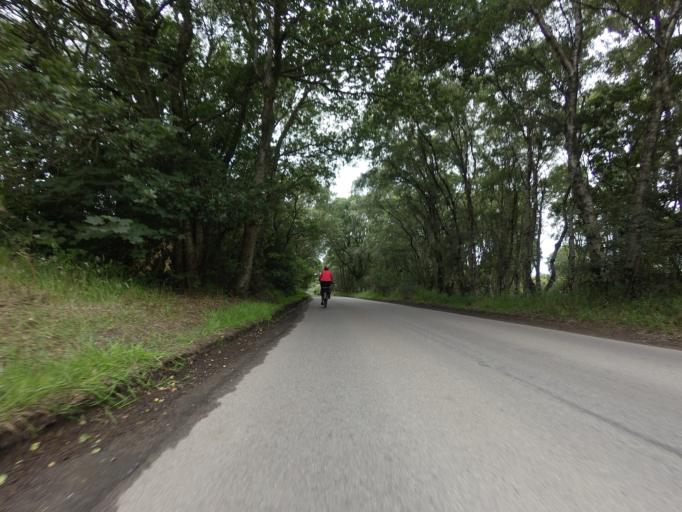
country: GB
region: Scotland
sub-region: Moray
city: Elgin
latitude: 57.6551
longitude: -3.3473
